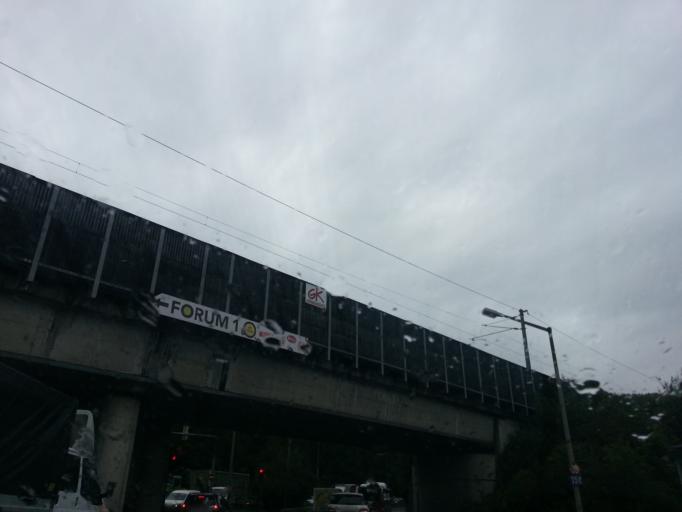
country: AT
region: Salzburg
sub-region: Politischer Bezirk Salzburg-Umgebung
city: Bergheim
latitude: 47.8258
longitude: 13.0545
